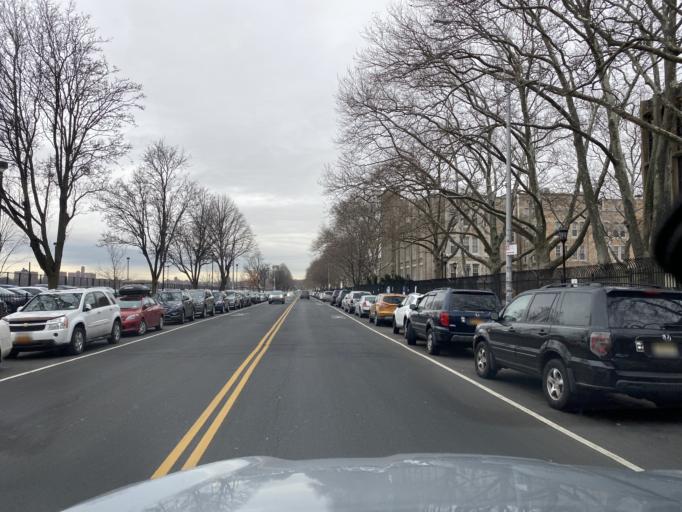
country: US
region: New York
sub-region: New York County
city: Inwood
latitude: 40.8718
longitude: -73.8971
